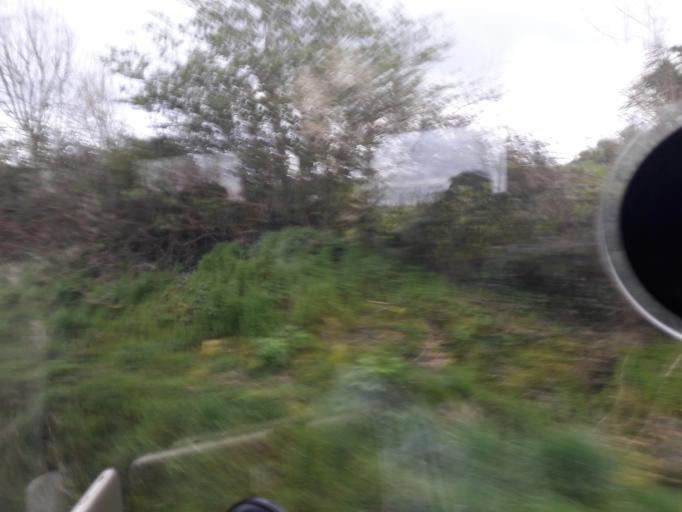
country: IE
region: Leinster
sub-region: An Iarmhi
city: Rathwire
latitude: 53.4943
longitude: -7.1878
